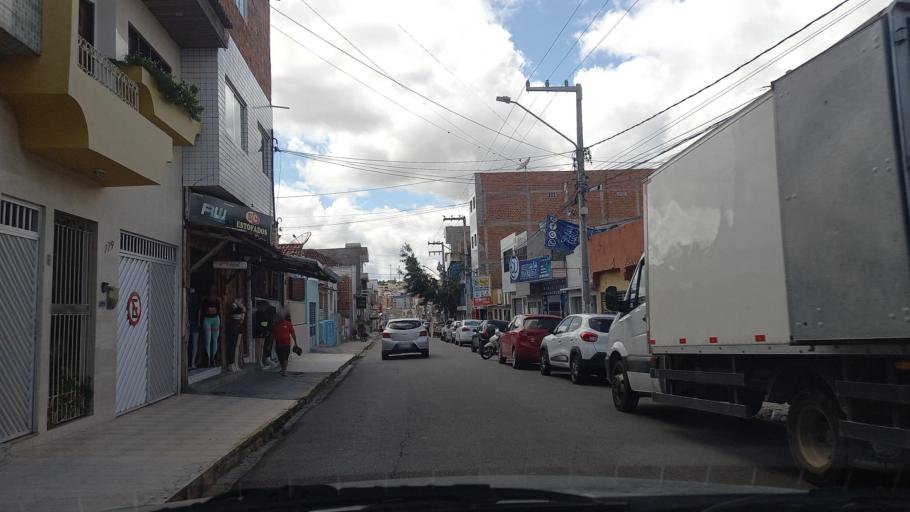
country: BR
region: Pernambuco
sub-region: Caruaru
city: Caruaru
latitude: -8.2846
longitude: -35.9652
